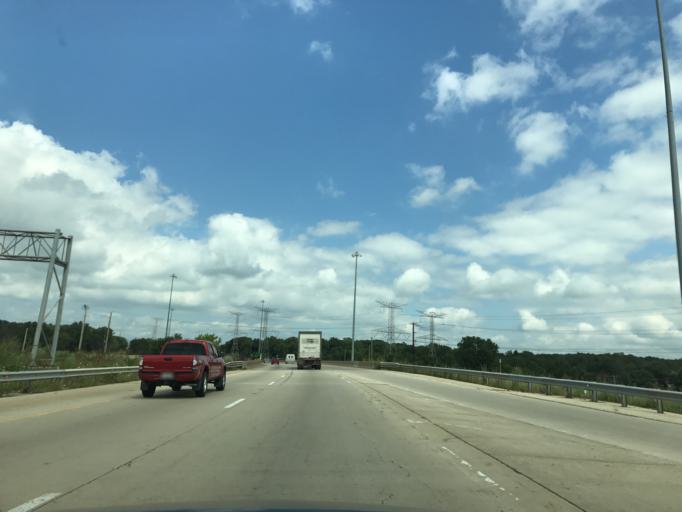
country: US
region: Illinois
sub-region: Will County
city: New Lenox
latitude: 41.5190
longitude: -87.9924
